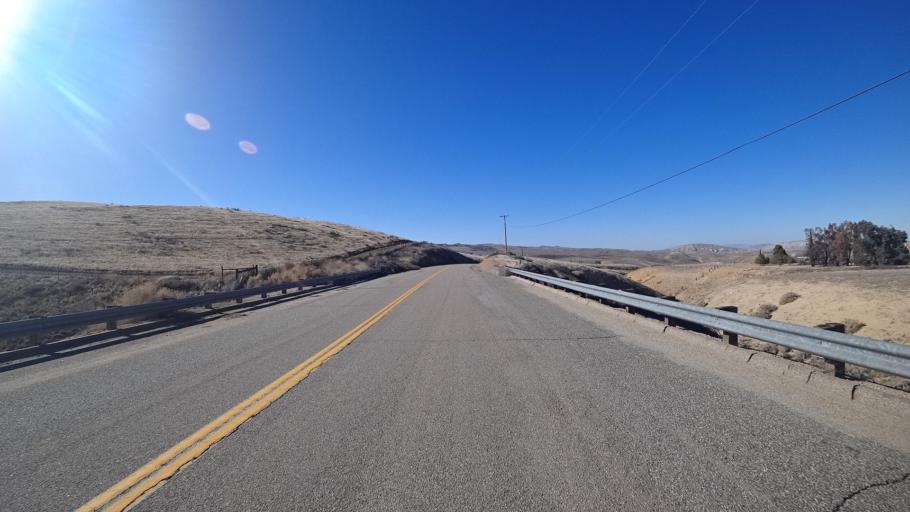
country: US
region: California
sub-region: Kern County
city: Maricopa
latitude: 34.9587
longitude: -119.4433
